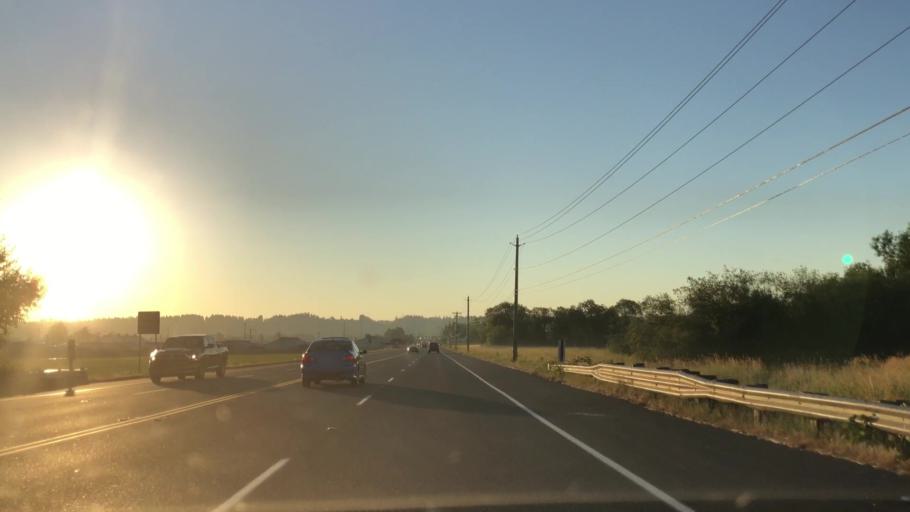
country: US
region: Washington
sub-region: King County
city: Lakeland North
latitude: 47.3537
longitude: -122.2584
